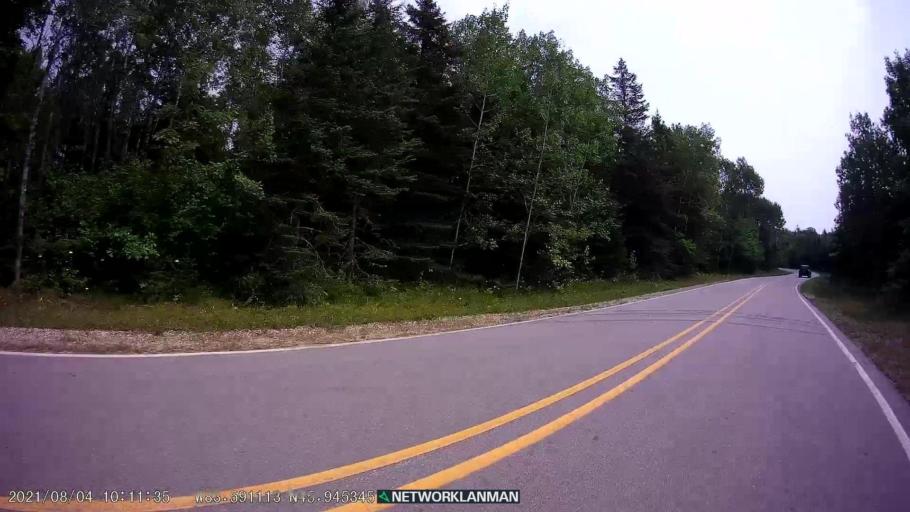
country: CA
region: Ontario
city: Thessalon
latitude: 45.9452
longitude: -83.5907
